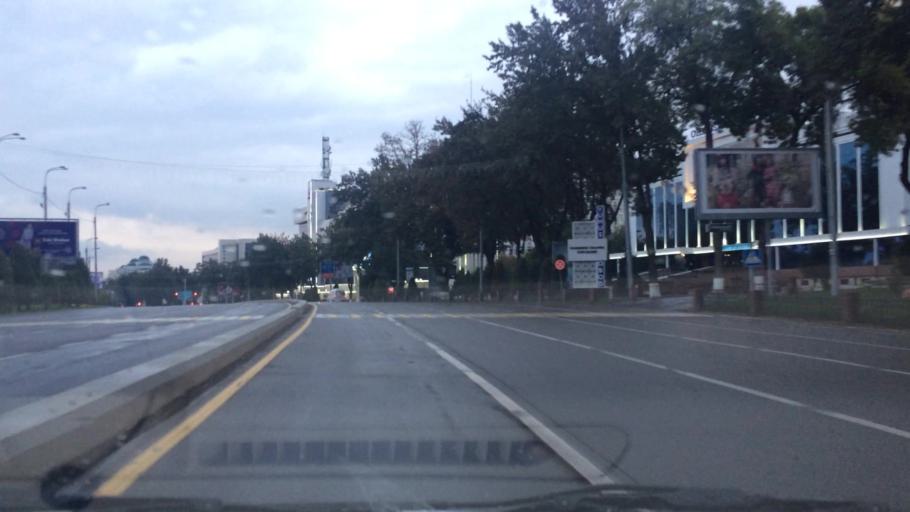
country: UZ
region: Toshkent Shahri
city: Tashkent
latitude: 41.3156
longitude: 69.2845
